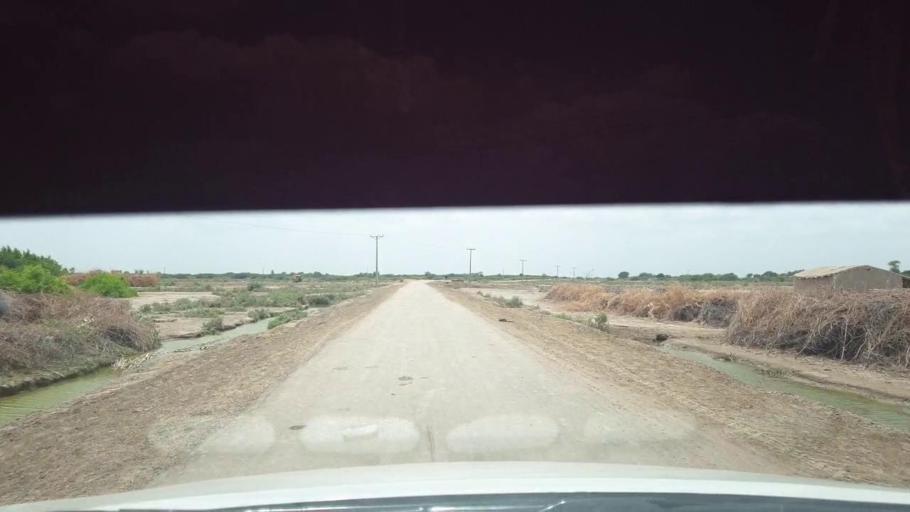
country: PK
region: Sindh
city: Kadhan
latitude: 24.5466
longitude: 69.1172
